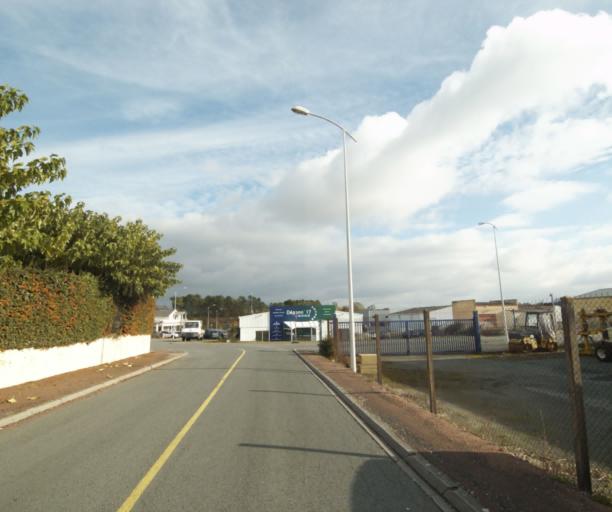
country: FR
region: Poitou-Charentes
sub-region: Departement de la Charente-Maritime
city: Saintes
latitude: 45.7518
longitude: -0.6762
